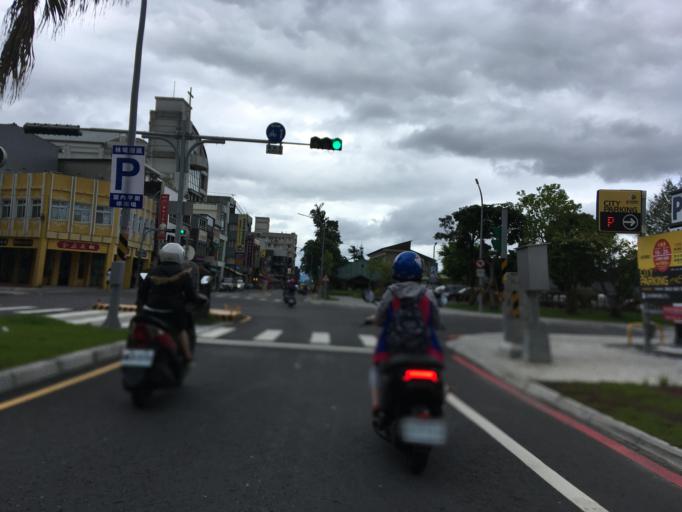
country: TW
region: Taiwan
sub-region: Yilan
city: Yilan
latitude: 24.6817
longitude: 121.7716
